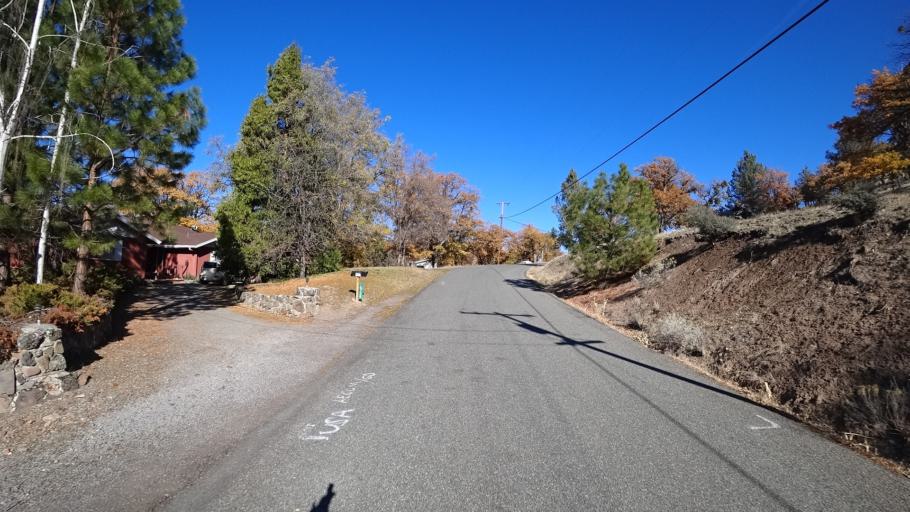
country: US
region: California
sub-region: Siskiyou County
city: Montague
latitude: 41.9769
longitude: -122.3196
